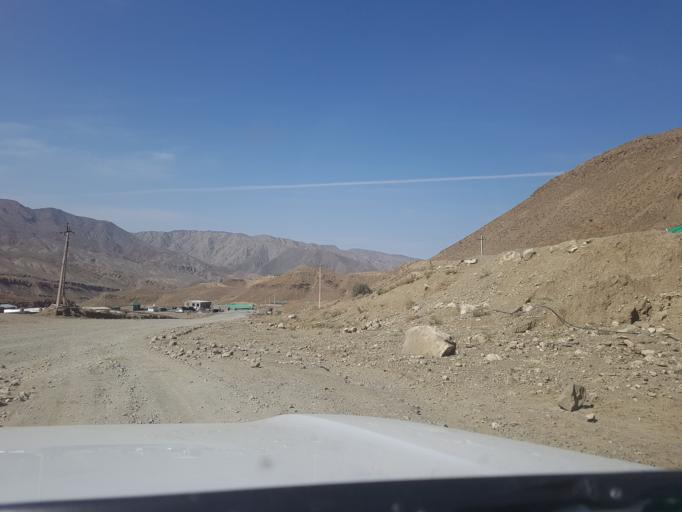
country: TM
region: Ahal
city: Baharly
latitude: 38.4524
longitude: 57.0458
